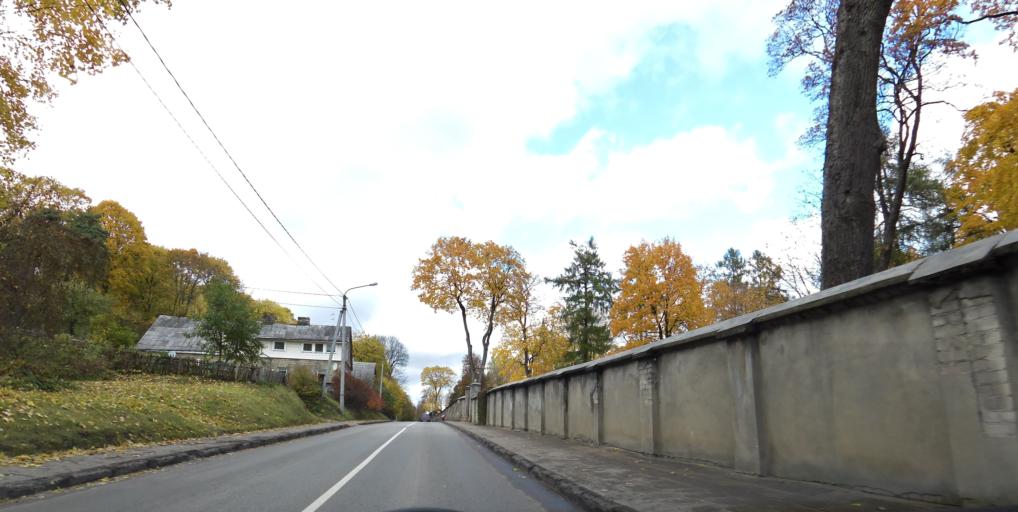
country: LT
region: Vilnius County
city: Rasos
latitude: 54.6678
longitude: 25.3036
